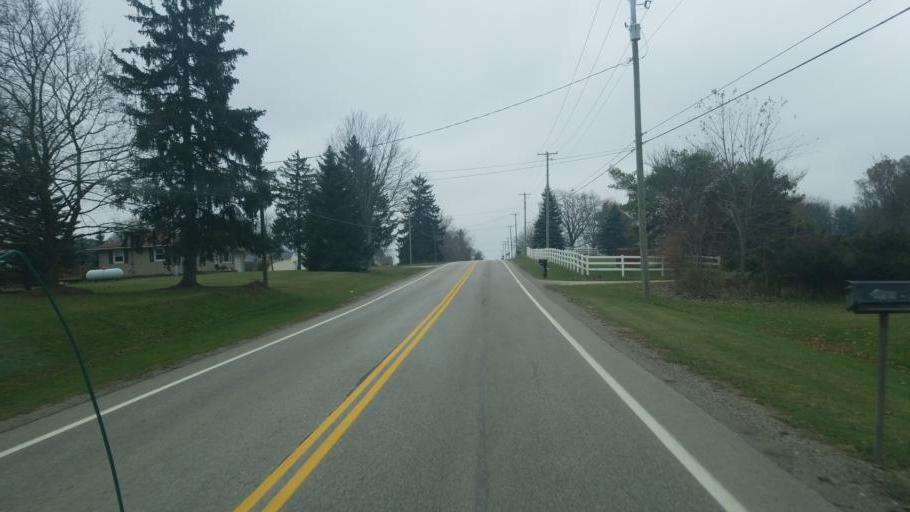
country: US
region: Ohio
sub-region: Medina County
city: Medina
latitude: 41.1388
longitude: -81.9236
